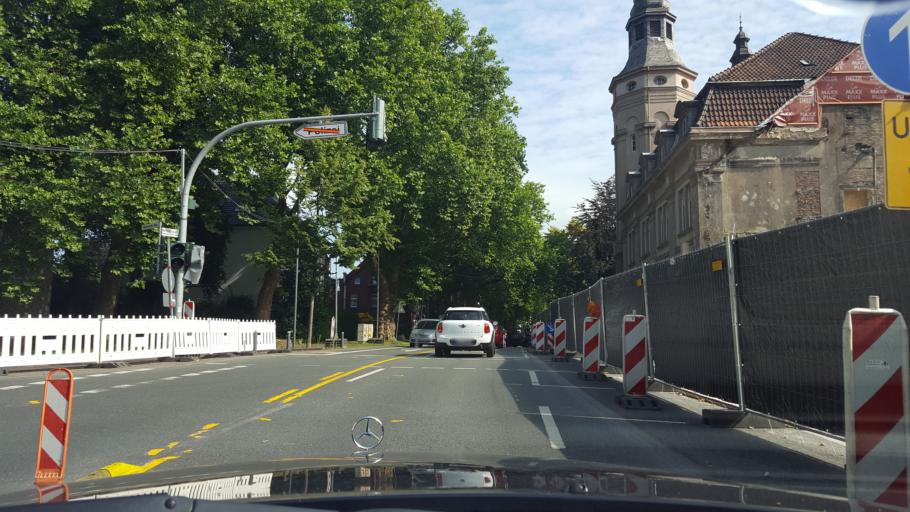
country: DE
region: North Rhine-Westphalia
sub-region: Regierungsbezirk Munster
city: Recklinghausen
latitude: 51.6137
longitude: 7.1933
